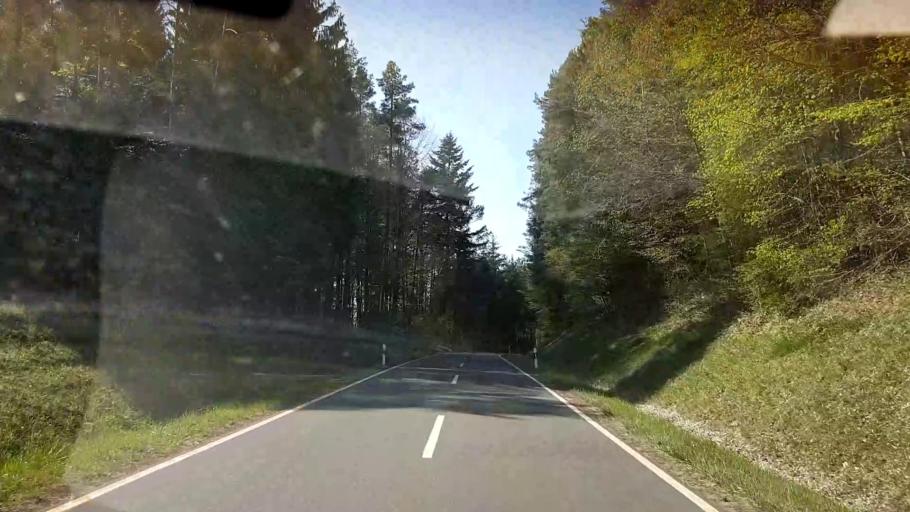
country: DE
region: Bavaria
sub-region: Upper Franconia
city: Pottenstein
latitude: 49.7932
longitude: 11.4107
